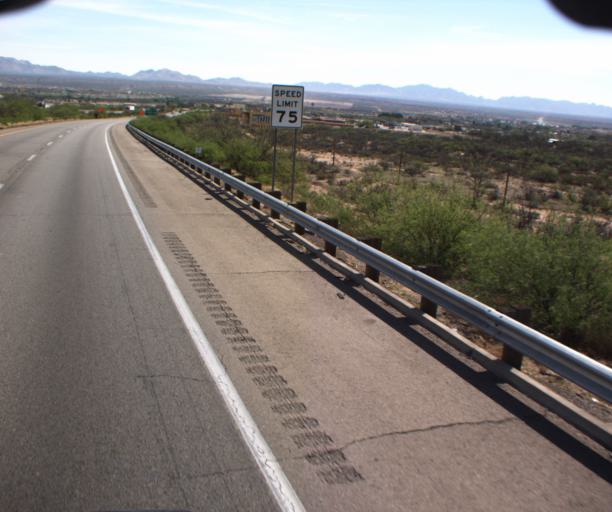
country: US
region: Arizona
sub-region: Cochise County
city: Benson
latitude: 31.9768
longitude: -110.3148
